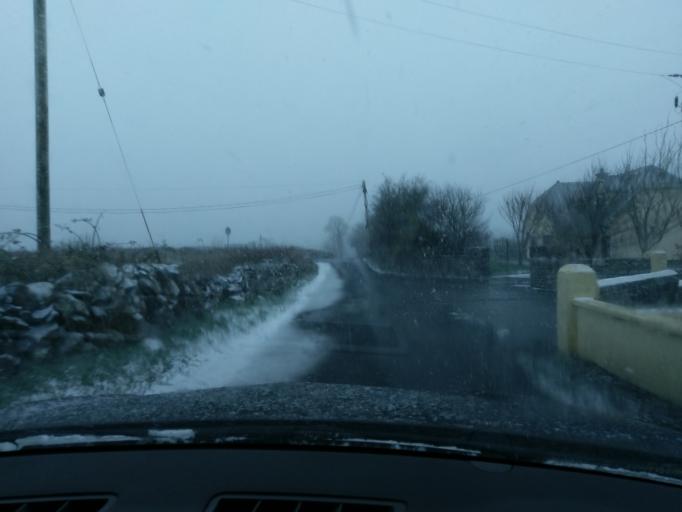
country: IE
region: Connaught
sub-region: County Galway
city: Oranmore
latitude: 53.2015
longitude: -8.9007
